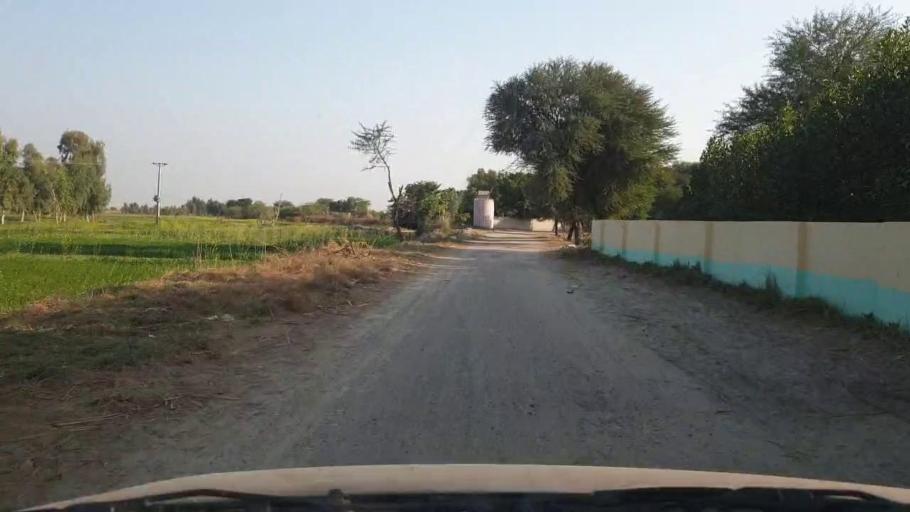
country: PK
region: Sindh
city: Samaro
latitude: 25.2738
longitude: 69.3632
